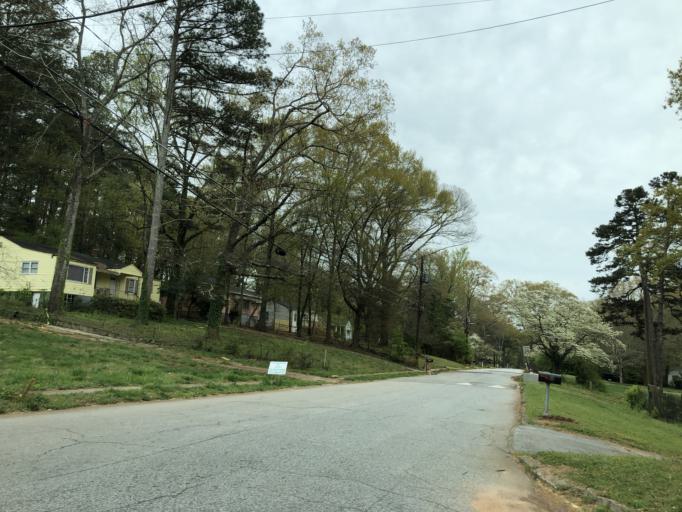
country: US
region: Georgia
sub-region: DeKalb County
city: Belvedere Park
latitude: 33.7533
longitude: -84.2543
